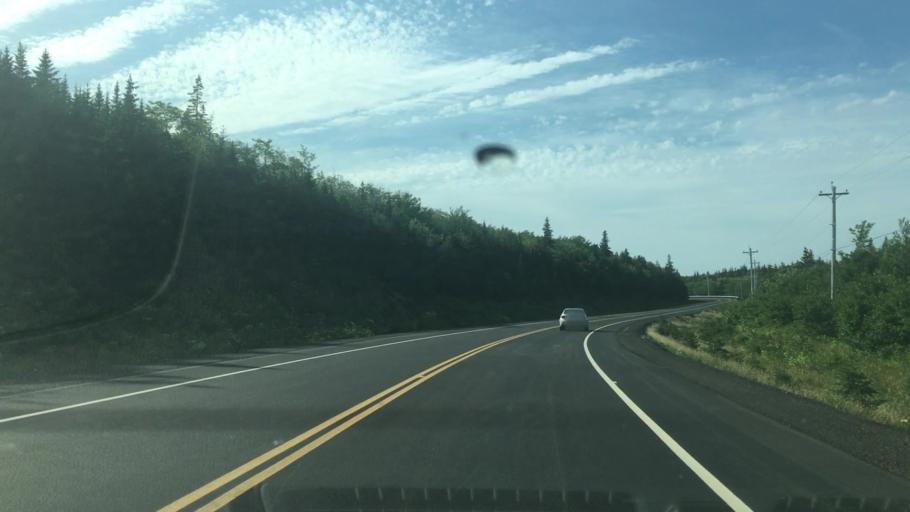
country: CA
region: Nova Scotia
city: Sydney Mines
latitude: 46.8377
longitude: -60.3846
